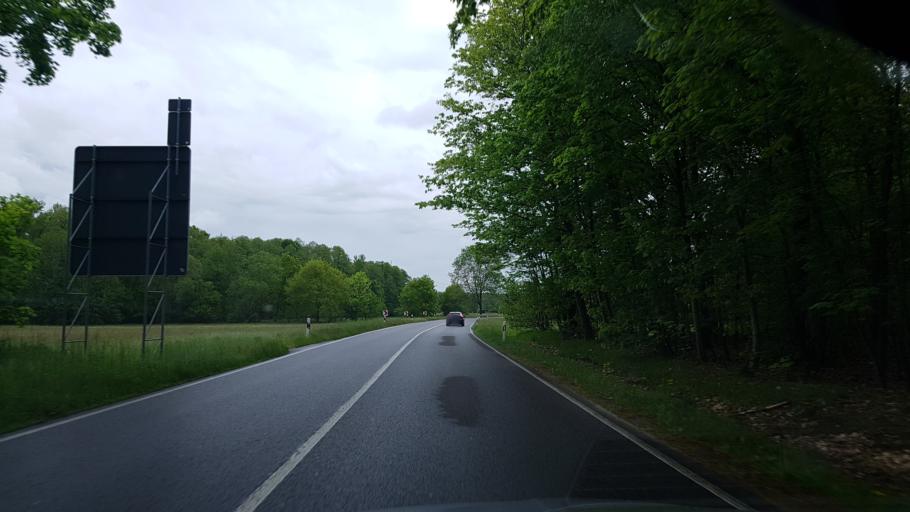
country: DE
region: Brandenburg
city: Luebben
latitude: 51.9012
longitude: 13.8203
